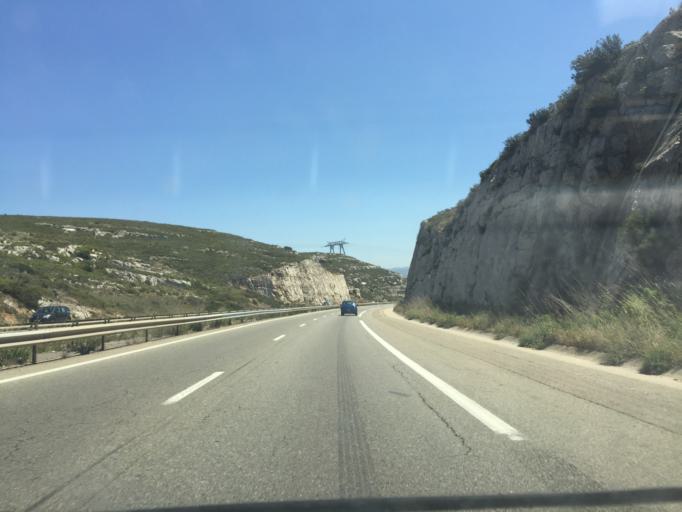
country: FR
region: Provence-Alpes-Cote d'Azur
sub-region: Departement des Bouches-du-Rhone
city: Les Pennes-Mirabeau
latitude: 43.3844
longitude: 5.3123
